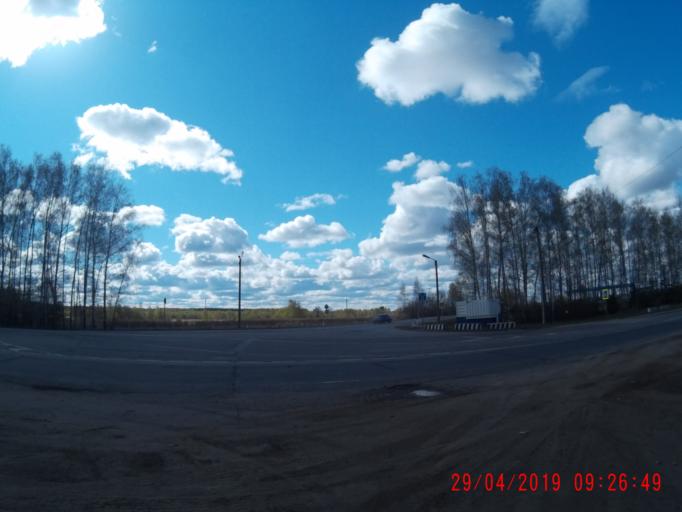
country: RU
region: Nizjnij Novgorod
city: Diveyevo
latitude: 55.0490
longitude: 43.2828
